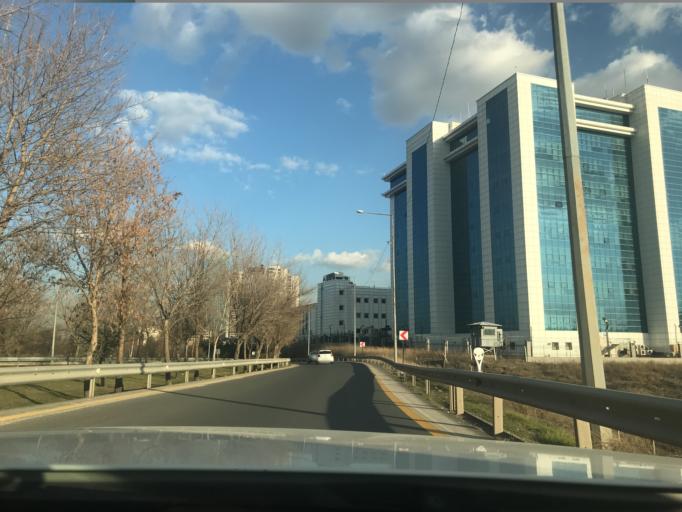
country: TR
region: Ankara
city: Batikent
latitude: 39.9171
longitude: 32.7785
